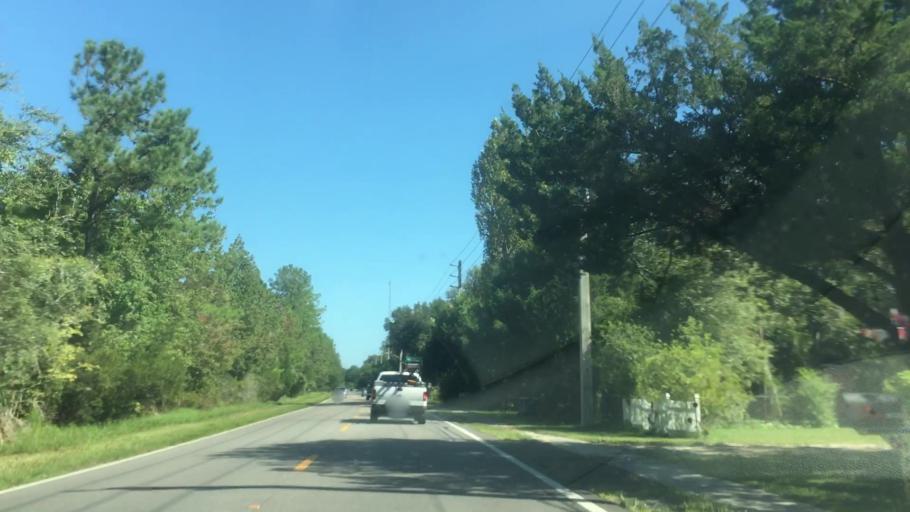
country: US
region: Florida
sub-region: Nassau County
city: Yulee
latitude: 30.4918
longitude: -81.5882
